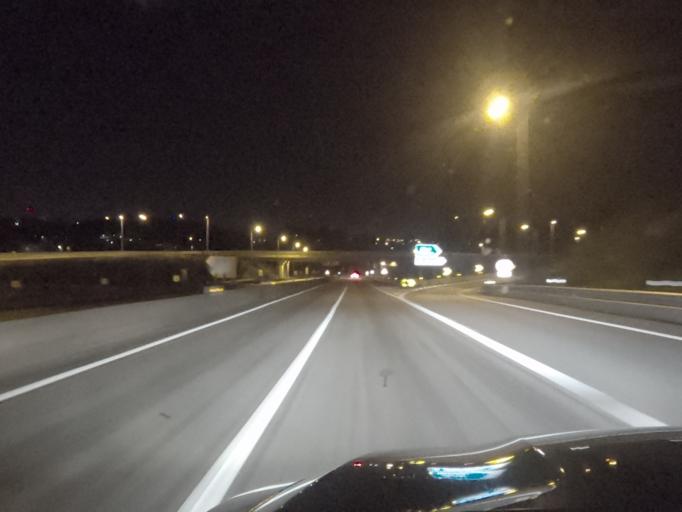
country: PT
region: Porto
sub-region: Vila Nova de Gaia
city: Perozinho
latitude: 41.0834
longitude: -8.5753
